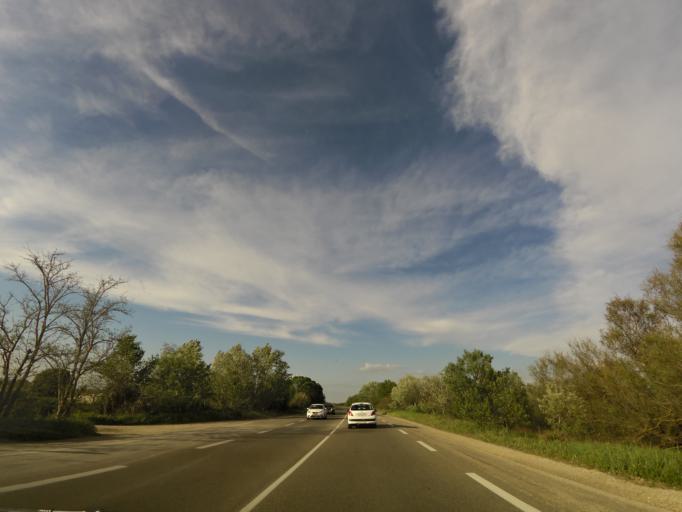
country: FR
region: Languedoc-Roussillon
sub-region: Departement de l'Herault
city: Candillargues
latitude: 43.6126
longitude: 4.1110
